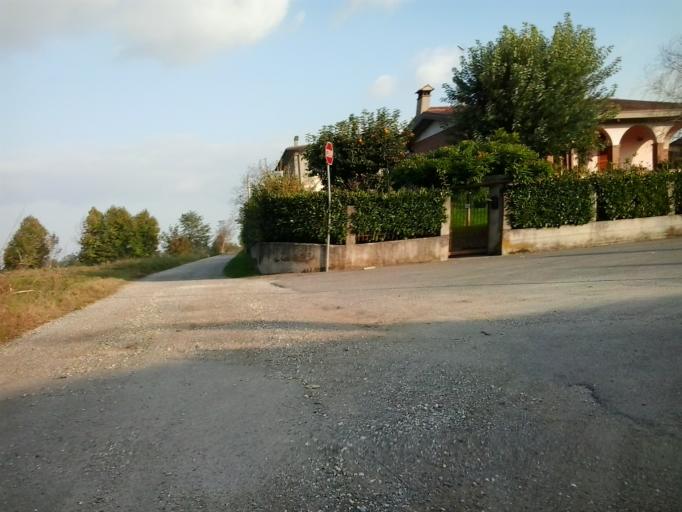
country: IT
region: Lombardy
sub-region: Provincia di Brescia
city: Azzano Mella
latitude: 45.4264
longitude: 10.1137
